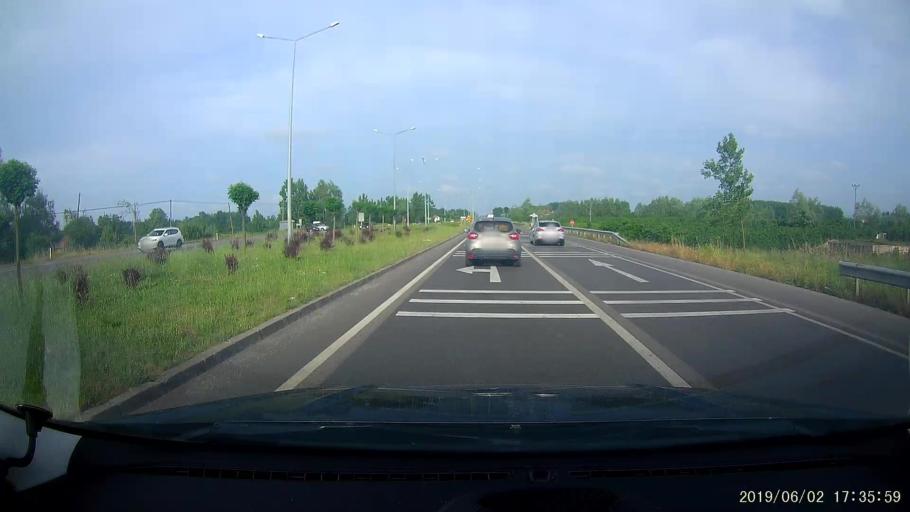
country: TR
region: Samsun
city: Terme
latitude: 41.2192
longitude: 36.8909
